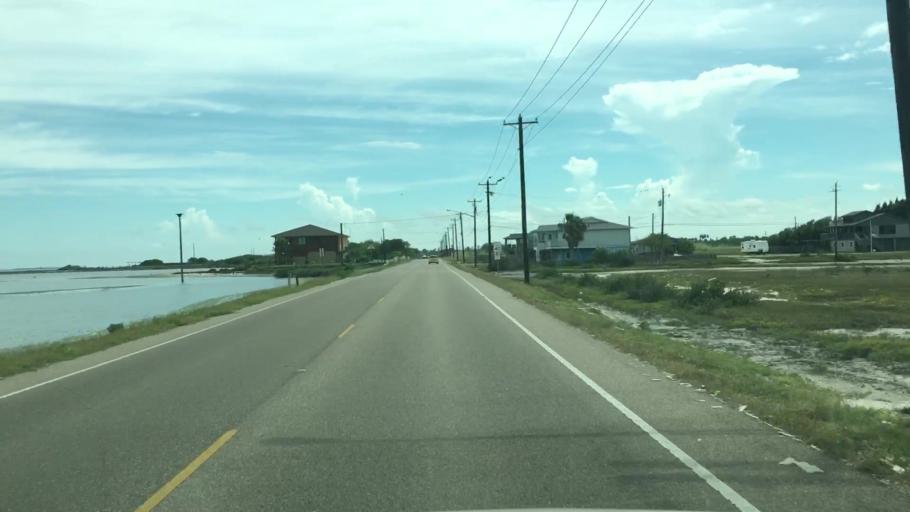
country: US
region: Texas
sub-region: Nueces County
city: Corpus Christi
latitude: 27.6488
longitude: -97.2815
